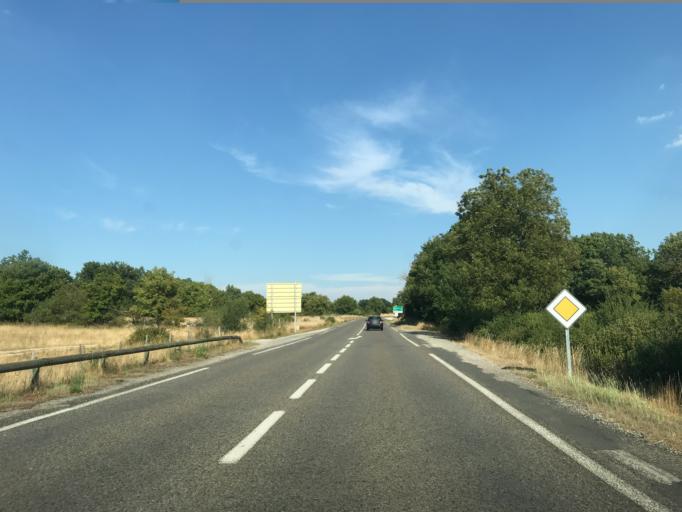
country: FR
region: Midi-Pyrenees
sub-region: Departement du Lot
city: Gramat
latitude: 44.6855
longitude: 1.6071
